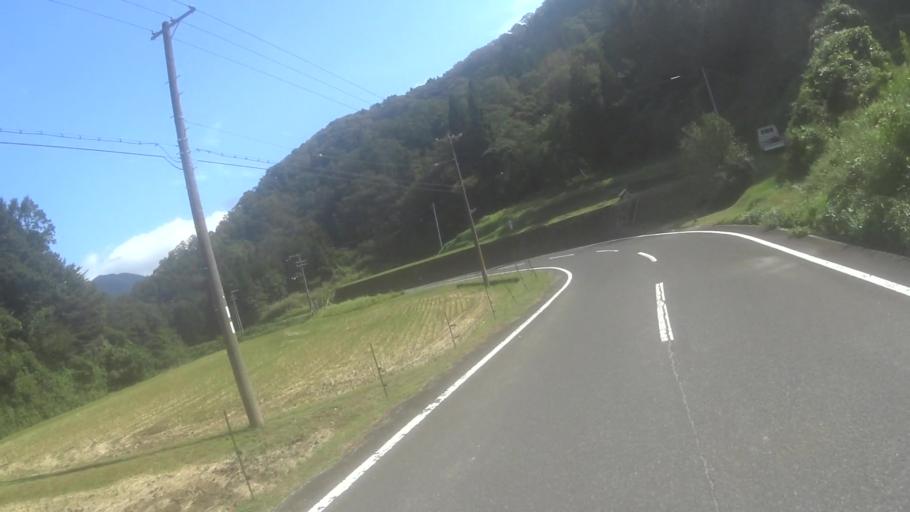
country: JP
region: Kyoto
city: Miyazu
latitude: 35.6755
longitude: 135.1519
